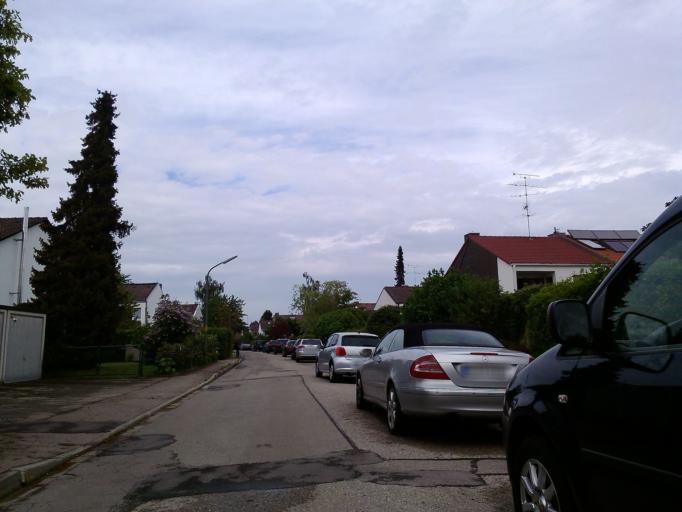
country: DE
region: Bavaria
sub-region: Upper Bavaria
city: Gauting
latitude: 48.0648
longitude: 11.3930
